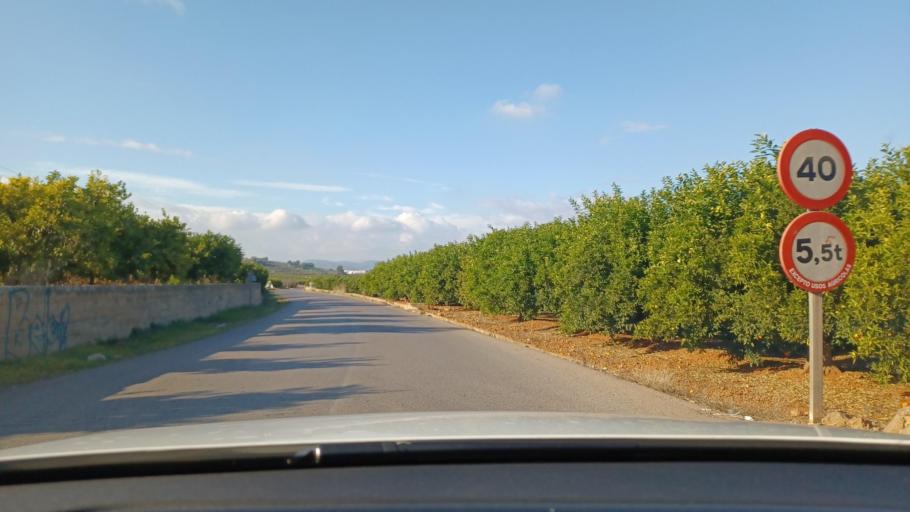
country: ES
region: Valencia
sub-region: Provincia de Castello
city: Betxi
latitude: 39.9342
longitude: -0.2045
